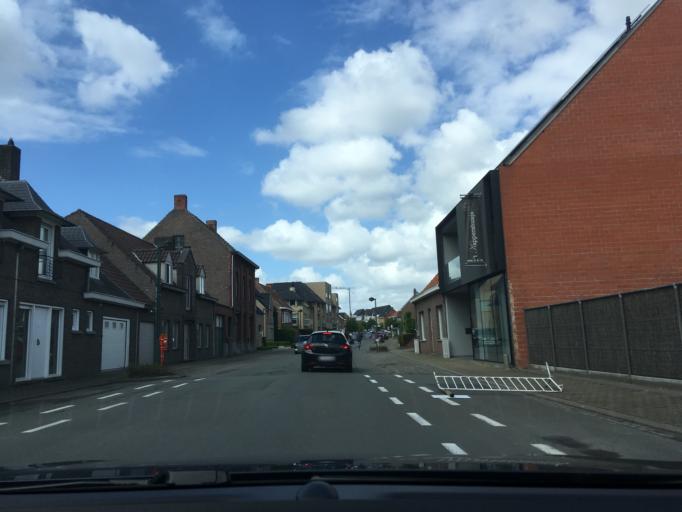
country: BE
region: Flanders
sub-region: Provincie West-Vlaanderen
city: Pittem
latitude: 50.9929
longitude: 3.2718
